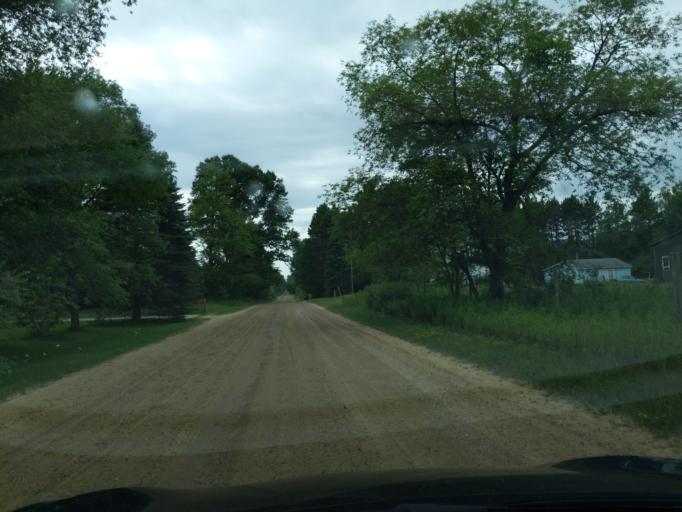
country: US
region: Michigan
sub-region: Clare County
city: Harrison
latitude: 44.0025
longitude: -84.9629
